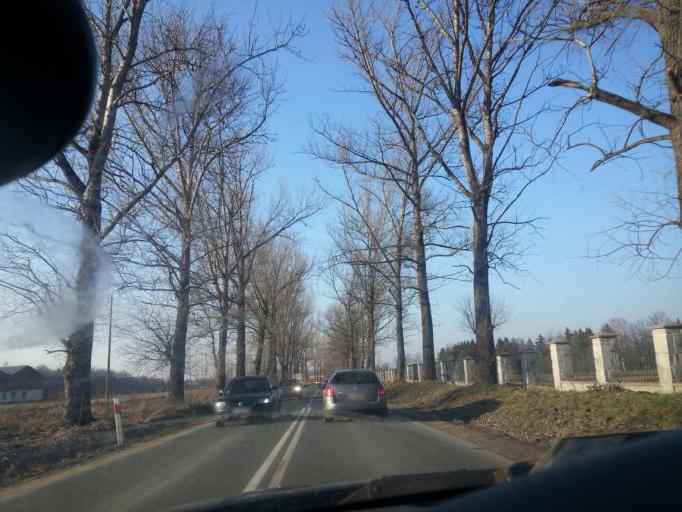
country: PL
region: Lower Silesian Voivodeship
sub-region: Powiat jeleniogorski
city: Myslakowice
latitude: 50.8372
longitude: 15.7880
